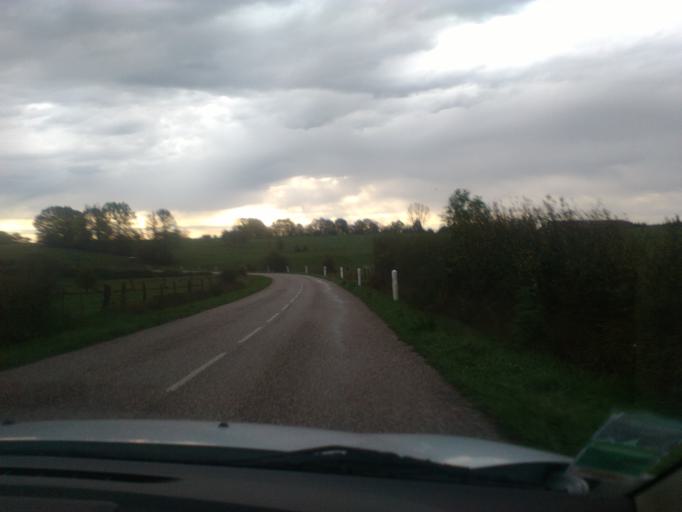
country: FR
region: Lorraine
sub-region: Departement des Vosges
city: Chavelot
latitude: 48.2831
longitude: 6.4603
